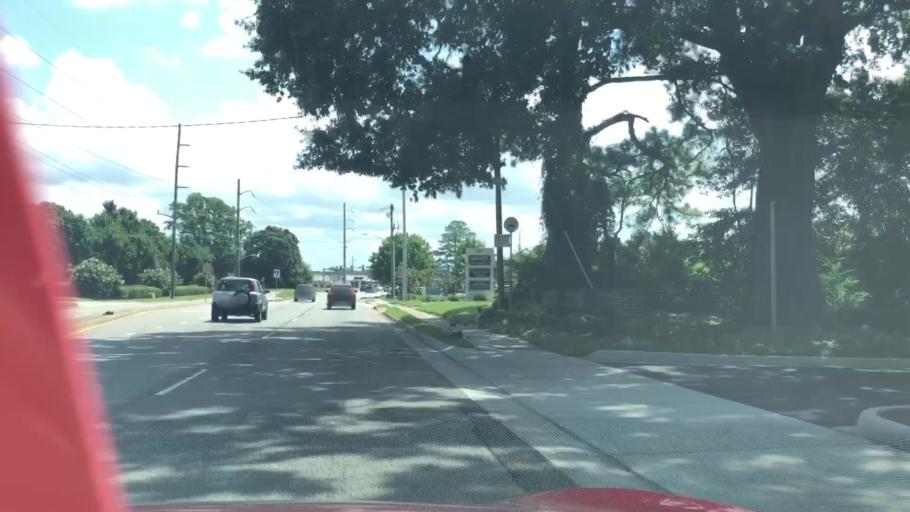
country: US
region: Virginia
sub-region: City of Virginia Beach
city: Virginia Beach
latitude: 36.8548
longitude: -76.0245
